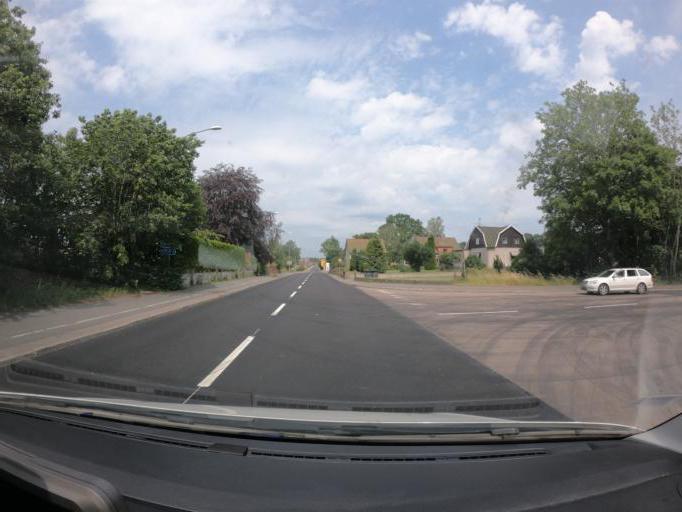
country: SE
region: Skane
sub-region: Hassleholms Kommun
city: Bjarnum
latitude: 56.2861
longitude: 13.7130
